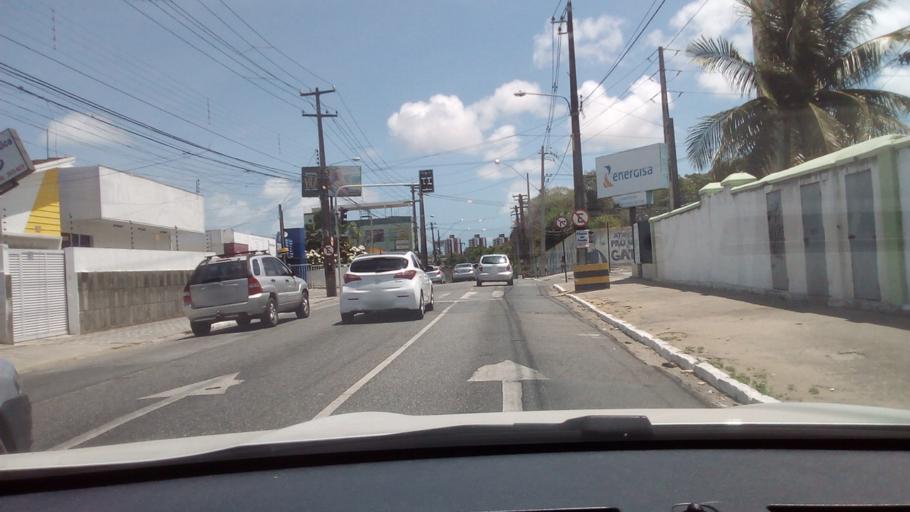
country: BR
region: Paraiba
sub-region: Joao Pessoa
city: Joao Pessoa
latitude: -7.1289
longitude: -34.8682
